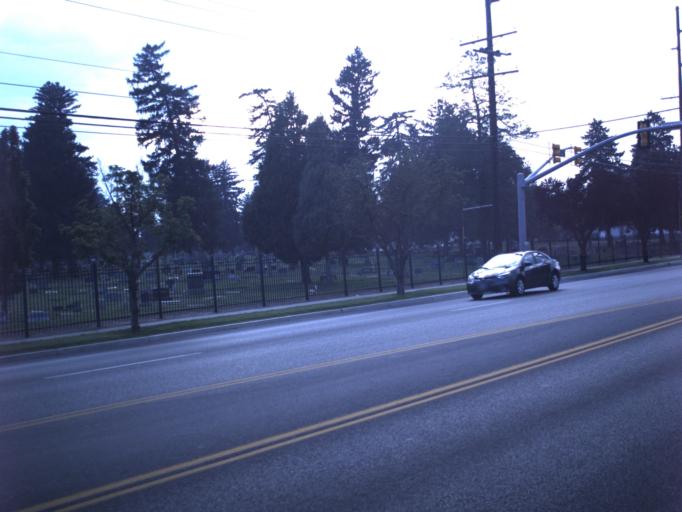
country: US
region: Utah
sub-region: Utah County
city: Provo
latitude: 40.2248
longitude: -111.6427
